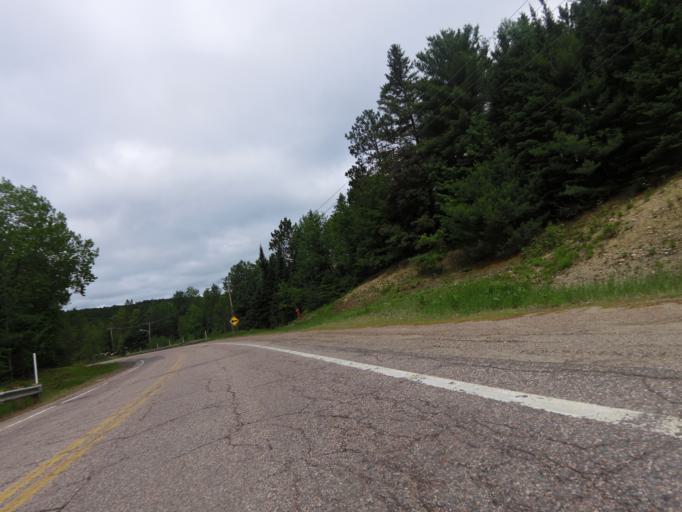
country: CA
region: Quebec
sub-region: Outaouais
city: Shawville
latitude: 45.8390
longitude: -76.4517
